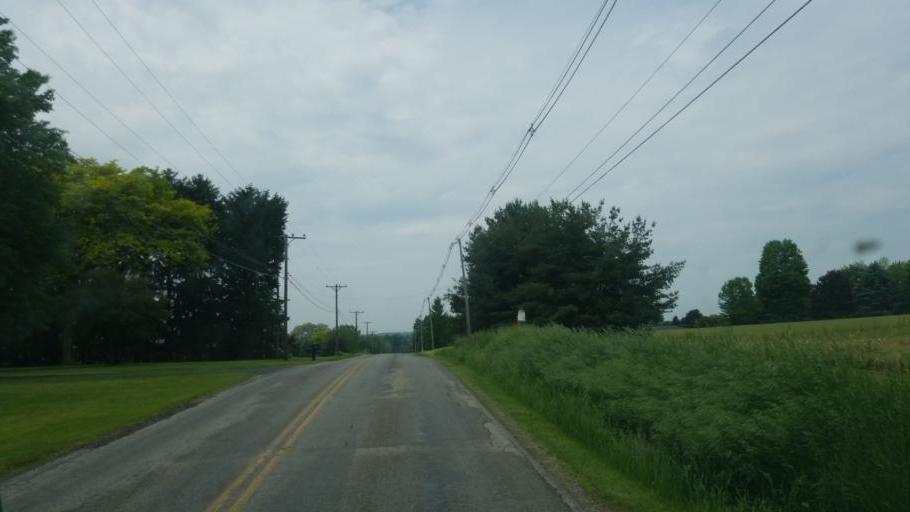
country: US
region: Ohio
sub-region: Wayne County
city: Orrville
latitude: 40.8220
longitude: -81.7591
